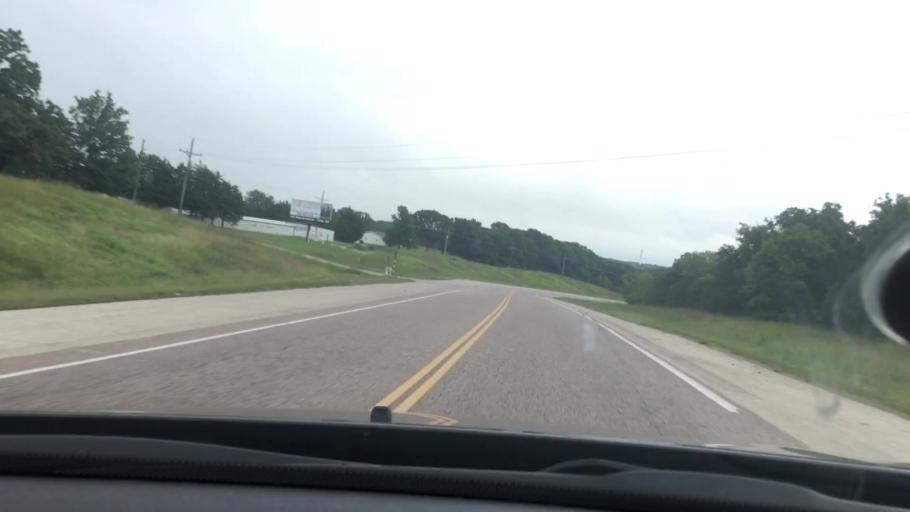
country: US
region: Oklahoma
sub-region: Pontotoc County
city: Ada
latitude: 34.7843
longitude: -96.5740
